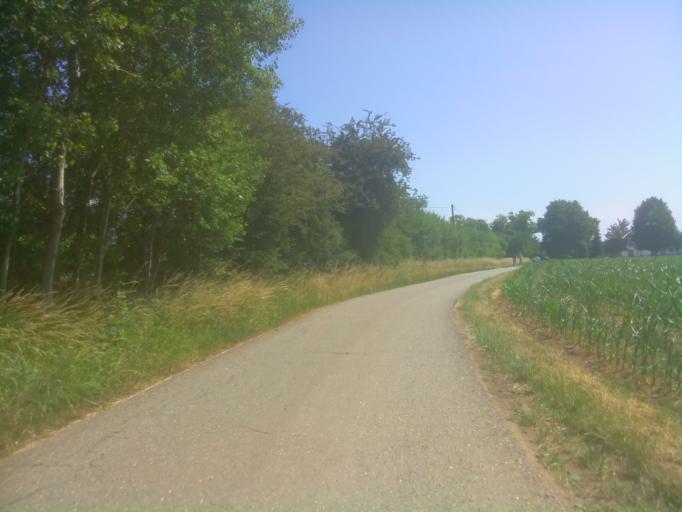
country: DE
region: Baden-Wuerttemberg
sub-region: Karlsruhe Region
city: Hemsbach
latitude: 49.5727
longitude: 8.6125
